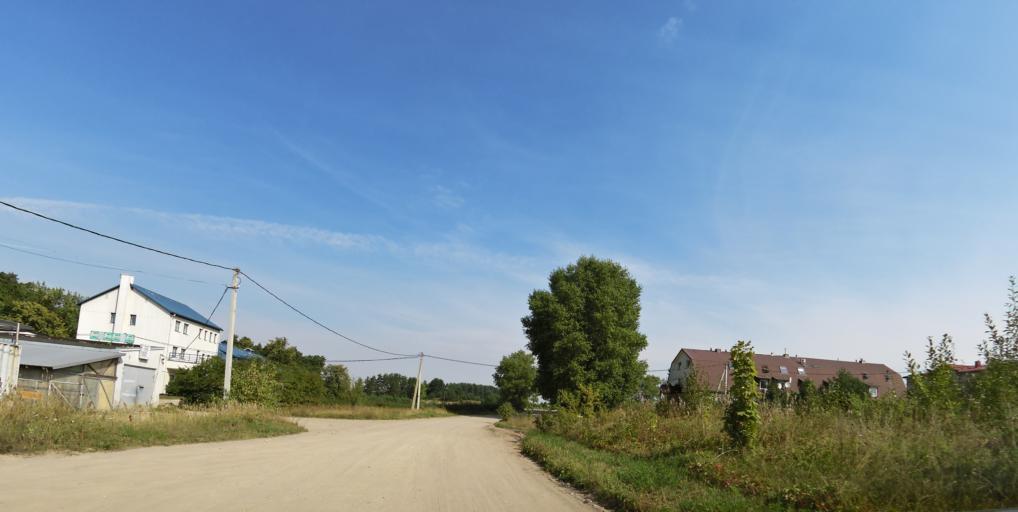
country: LT
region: Vilnius County
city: Pilaite
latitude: 54.7023
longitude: 25.1964
